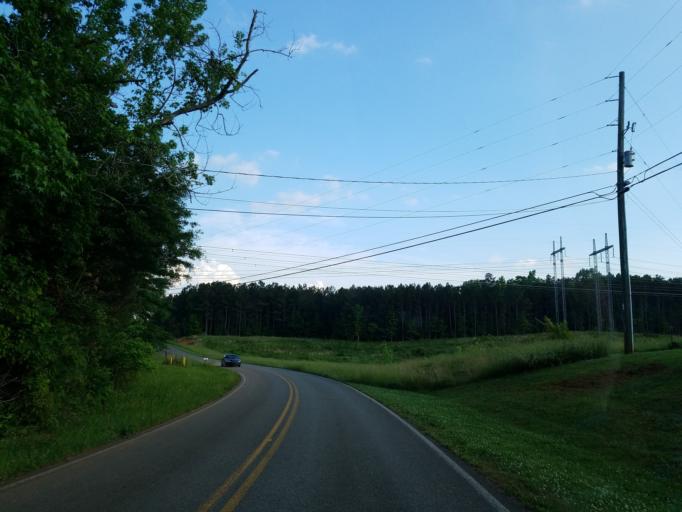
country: US
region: Georgia
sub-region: Cherokee County
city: Ball Ground
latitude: 34.3211
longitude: -84.3707
